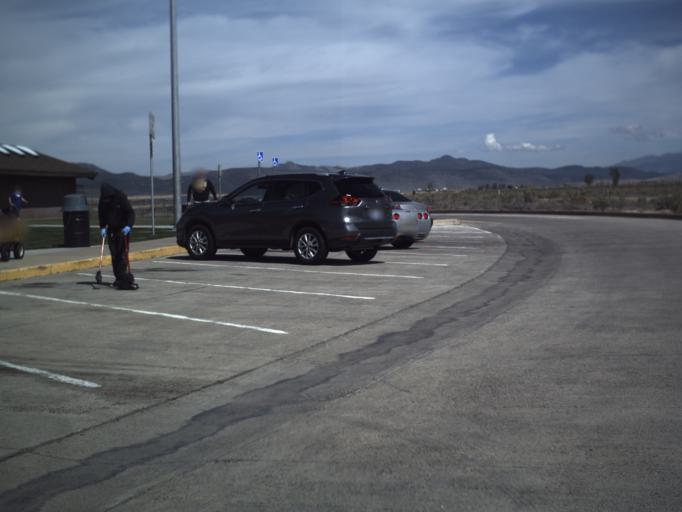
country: US
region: Utah
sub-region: Iron County
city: Parowan
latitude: 37.9803
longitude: -112.7358
